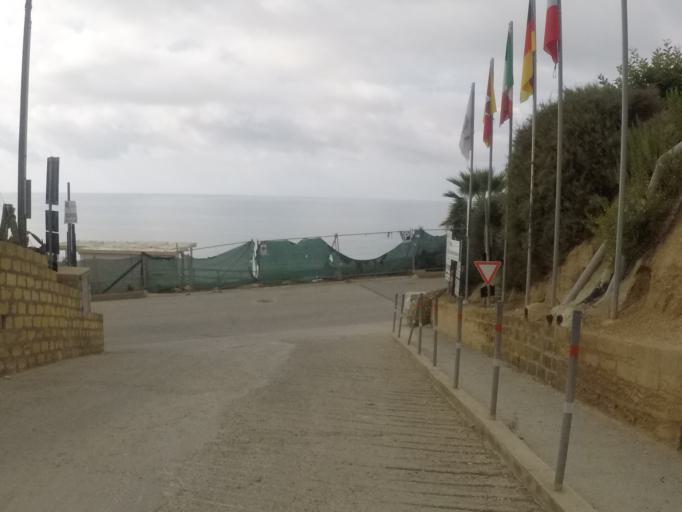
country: IT
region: Sicily
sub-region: Agrigento
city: Realmonte
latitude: 37.2893
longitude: 13.4787
